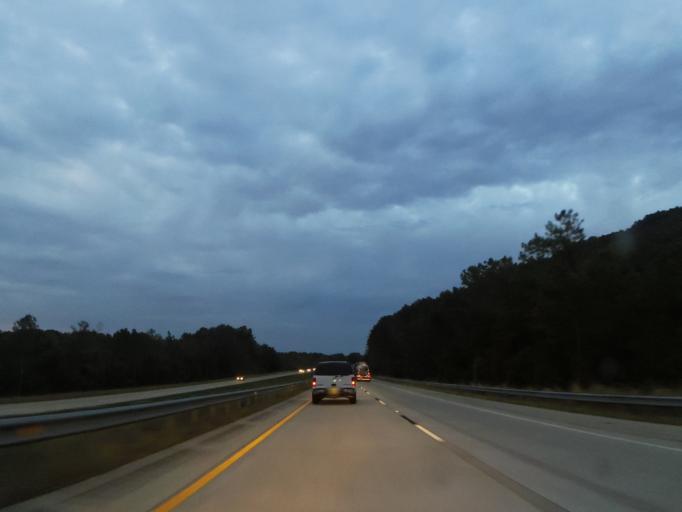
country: US
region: Alabama
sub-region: Etowah County
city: Whitesboro
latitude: 34.1446
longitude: -85.9884
